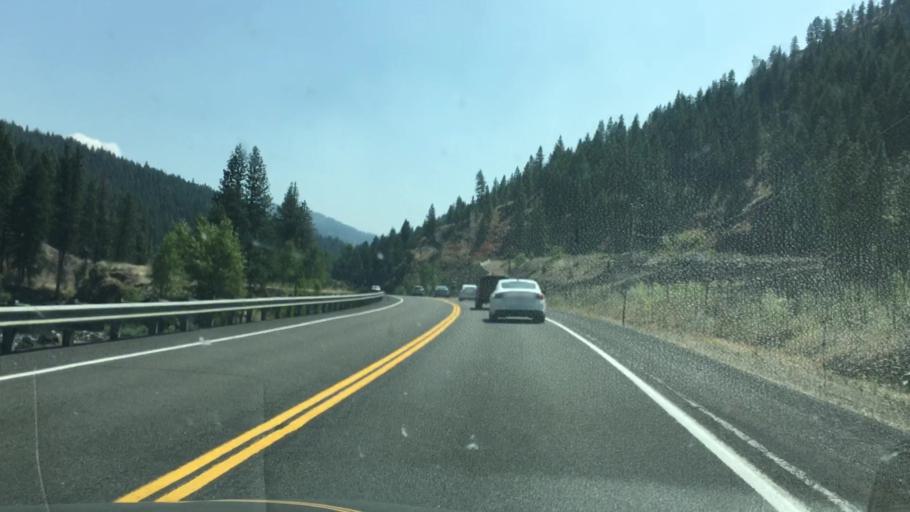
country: US
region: Idaho
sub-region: Valley County
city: McCall
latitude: 45.2188
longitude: -116.3181
